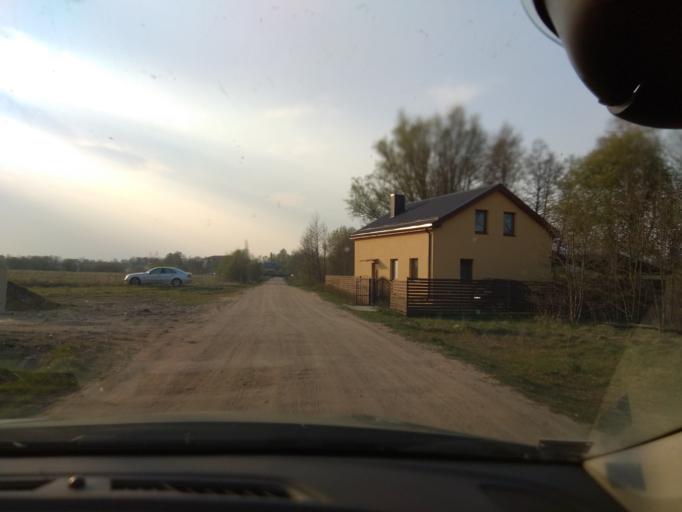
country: LT
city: Baltoji Voke
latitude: 54.5955
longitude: 25.1808
